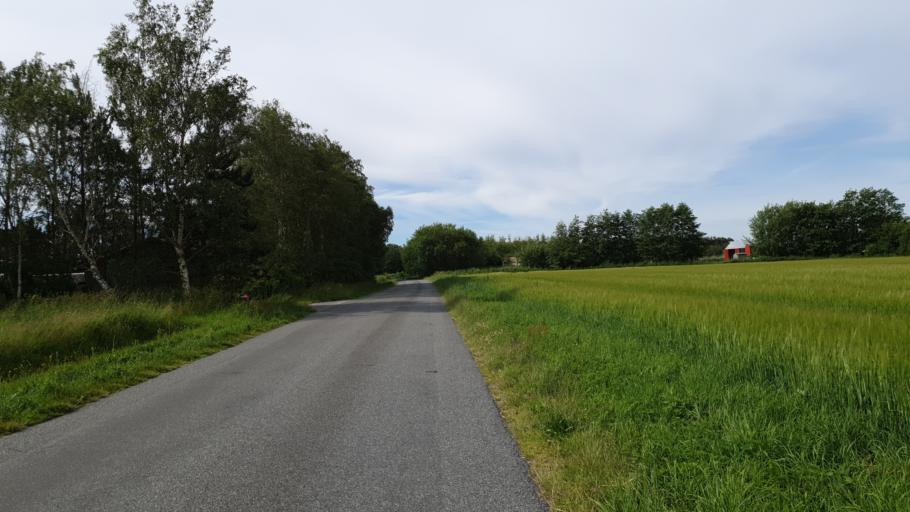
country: DK
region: North Denmark
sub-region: Laeso Kommune
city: Byrum
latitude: 57.2543
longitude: 10.9892
